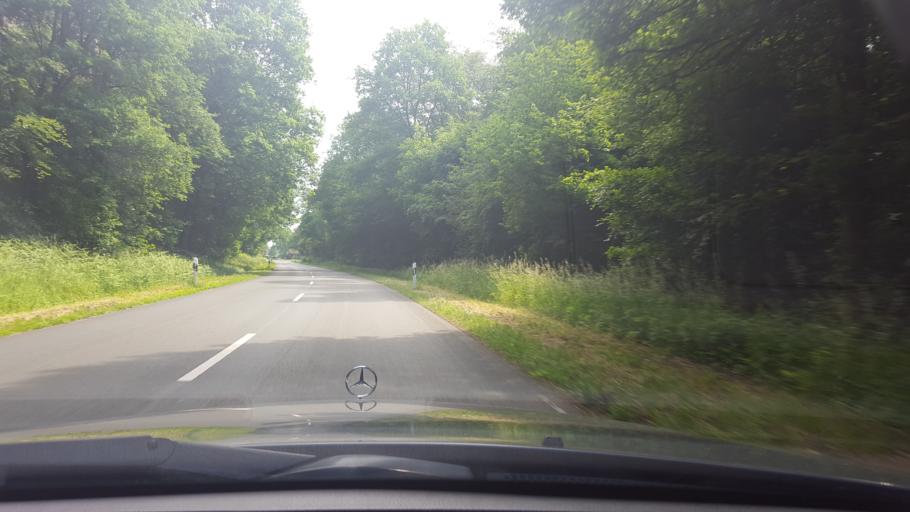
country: DE
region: North Rhine-Westphalia
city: Olfen
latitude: 51.7078
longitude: 7.3148
